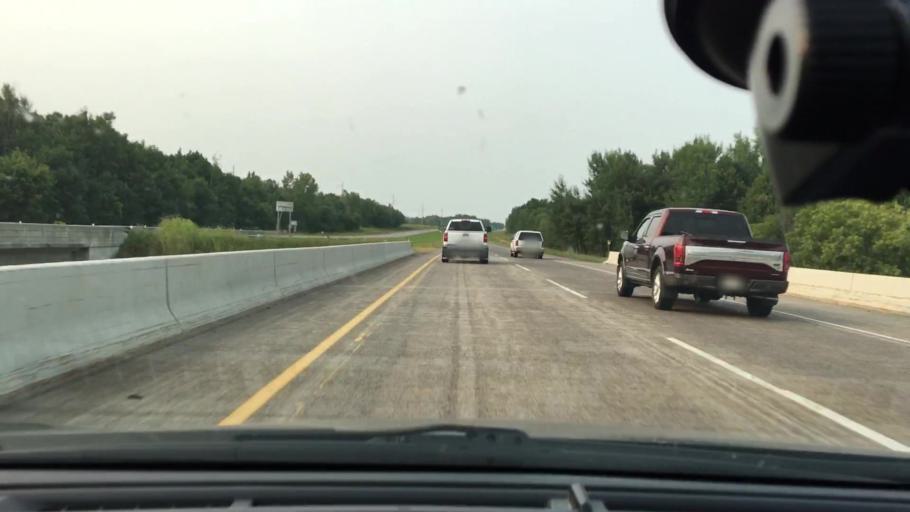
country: US
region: Minnesota
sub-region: Mille Lacs County
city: Milaca
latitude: 45.7335
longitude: -93.6395
